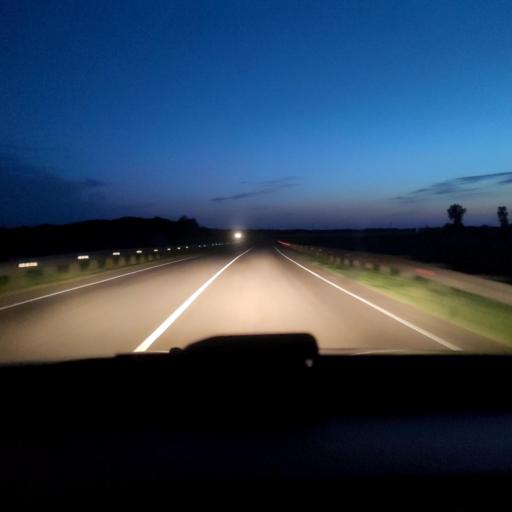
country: RU
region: Voronezj
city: Panino
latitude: 51.5738
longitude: 39.9130
